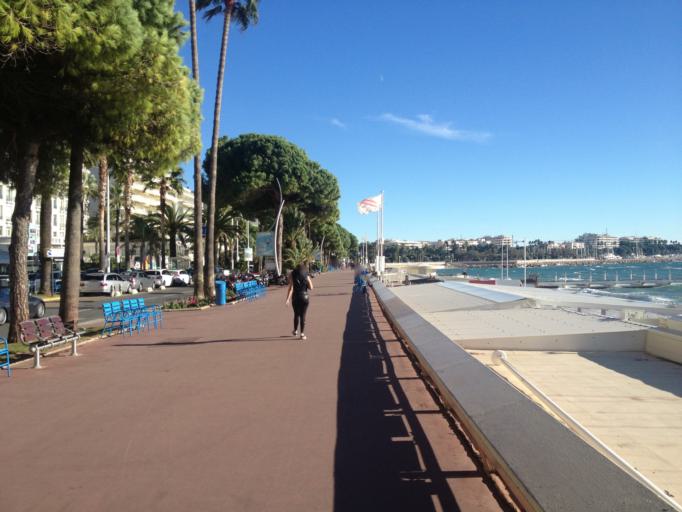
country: FR
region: Provence-Alpes-Cote d'Azur
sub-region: Departement des Alpes-Maritimes
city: Cannes
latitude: 43.5482
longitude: 7.0291
